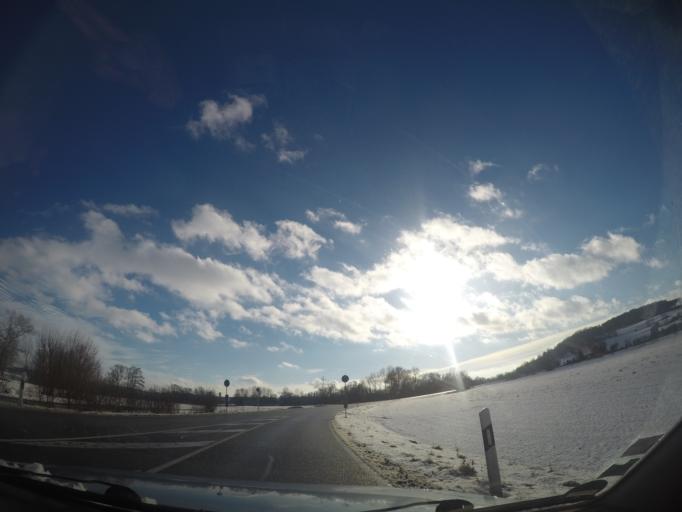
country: DE
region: Baden-Wuerttemberg
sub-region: Tuebingen Region
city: Dettingen
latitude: 48.2482
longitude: 9.7130
